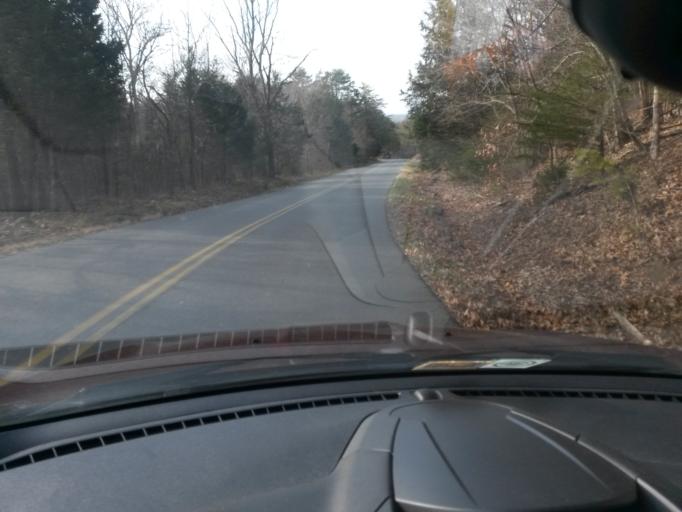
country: US
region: Virginia
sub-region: Botetourt County
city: Fincastle
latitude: 37.5499
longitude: -79.8763
